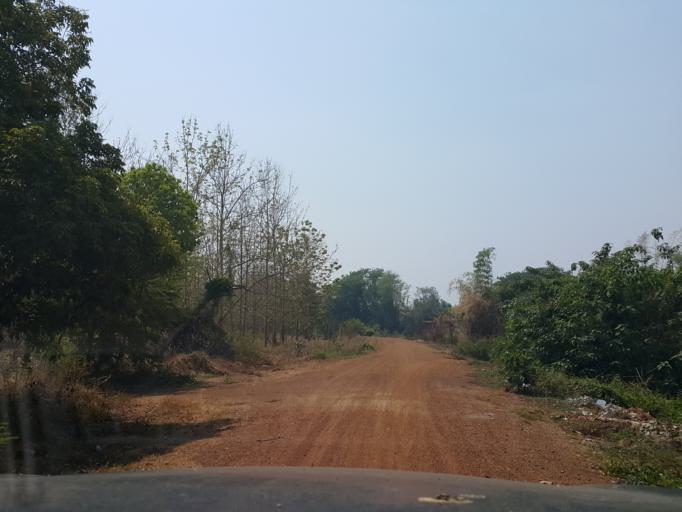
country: TH
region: Sukhothai
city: Thung Saliam
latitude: 17.3158
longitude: 99.5572
